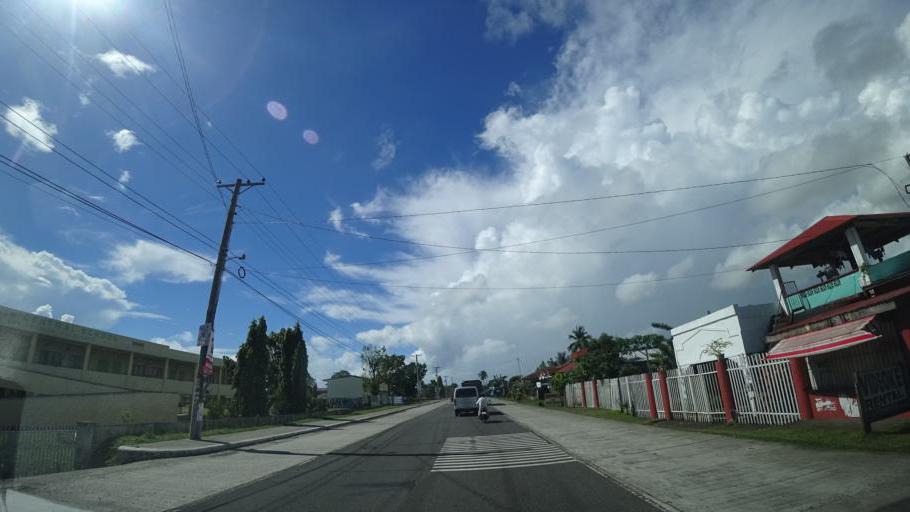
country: PH
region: Eastern Visayas
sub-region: Province of Leyte
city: Palo
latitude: 11.1425
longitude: 125.0041
